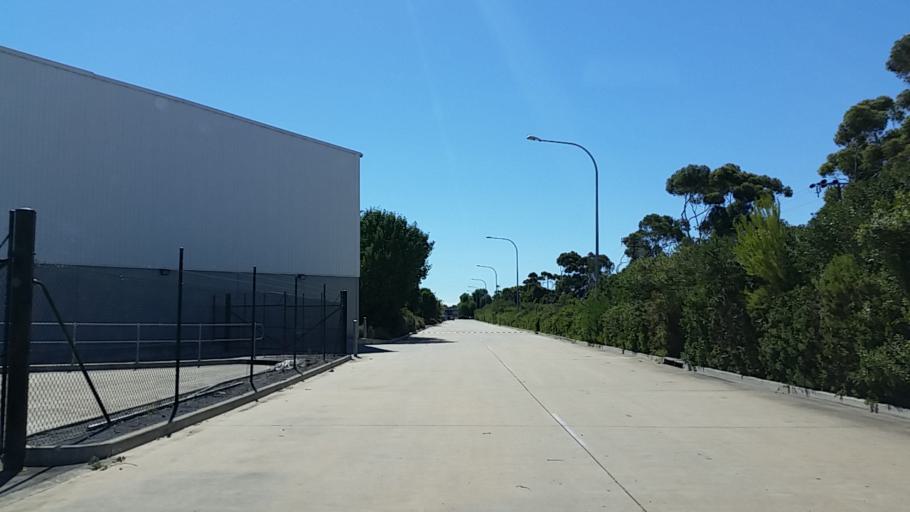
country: AU
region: South Australia
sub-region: Charles Sturt
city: Woodville North
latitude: -34.8750
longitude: 138.5349
